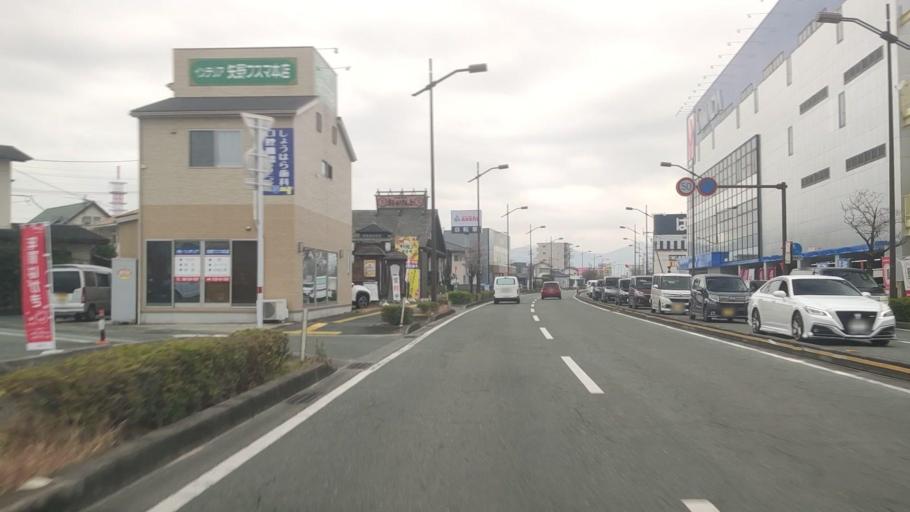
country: JP
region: Kumamoto
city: Kumamoto
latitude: 32.8049
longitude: 130.7561
